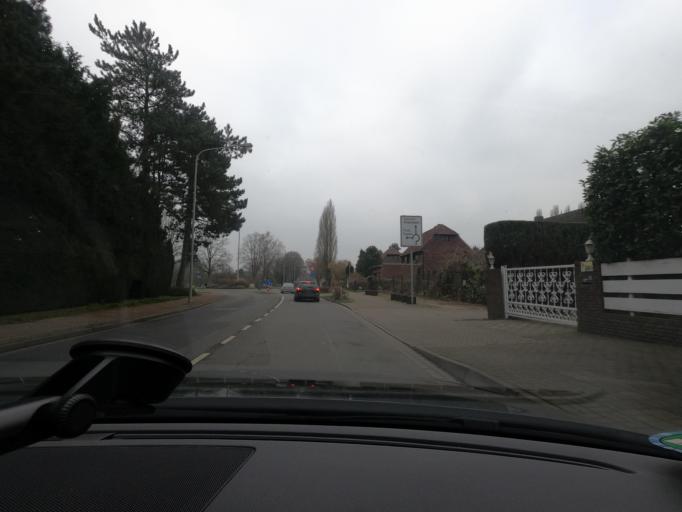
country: DE
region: North Rhine-Westphalia
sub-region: Regierungsbezirk Dusseldorf
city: Krefeld
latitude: 51.3637
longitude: 6.5691
